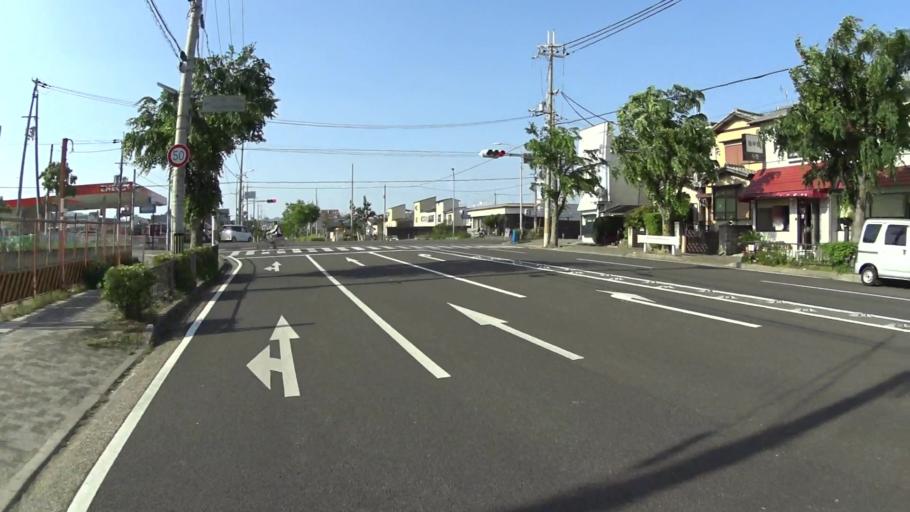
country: JP
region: Kyoto
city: Muko
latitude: 34.9393
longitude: 135.6911
